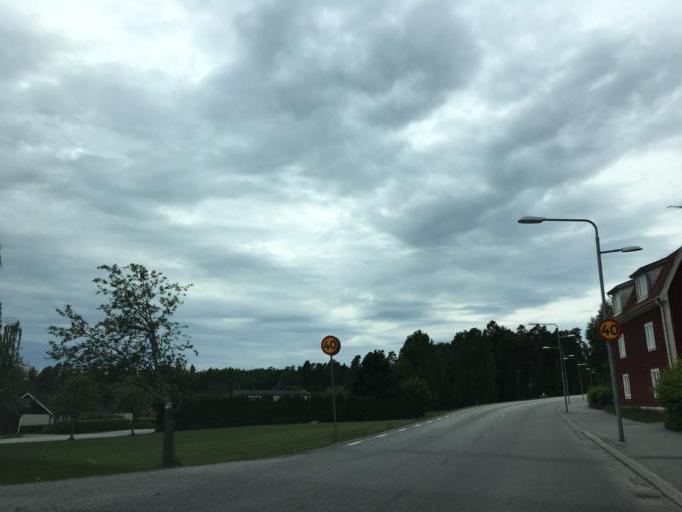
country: SE
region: Soedermanland
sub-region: Flens Kommun
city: Malmkoping
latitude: 59.1371
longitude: 16.7210
